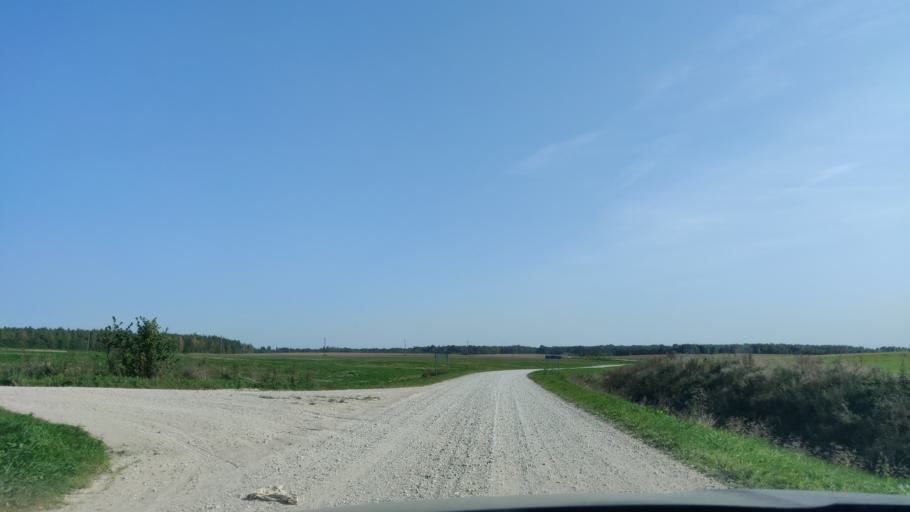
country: LT
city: Sirvintos
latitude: 54.9699
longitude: 24.8398
